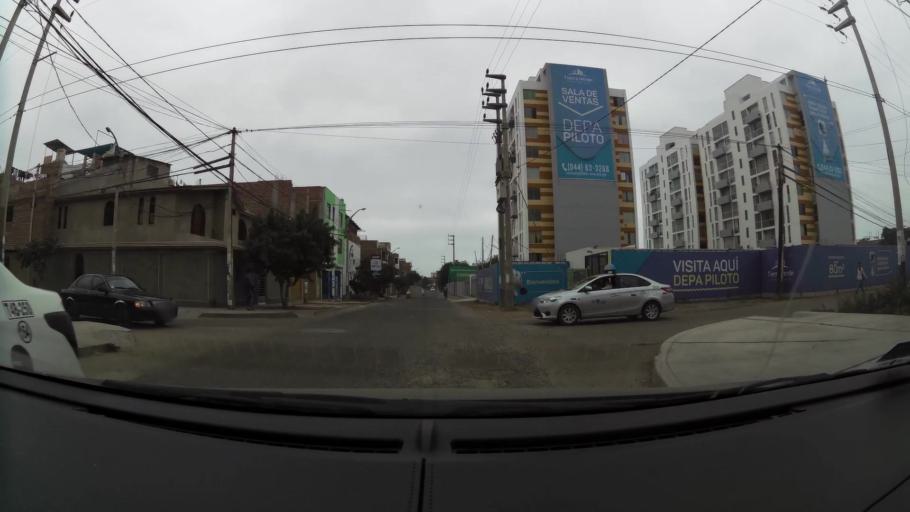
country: PE
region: La Libertad
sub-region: Provincia de Trujillo
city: Trujillo
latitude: -8.1093
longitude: -79.0444
